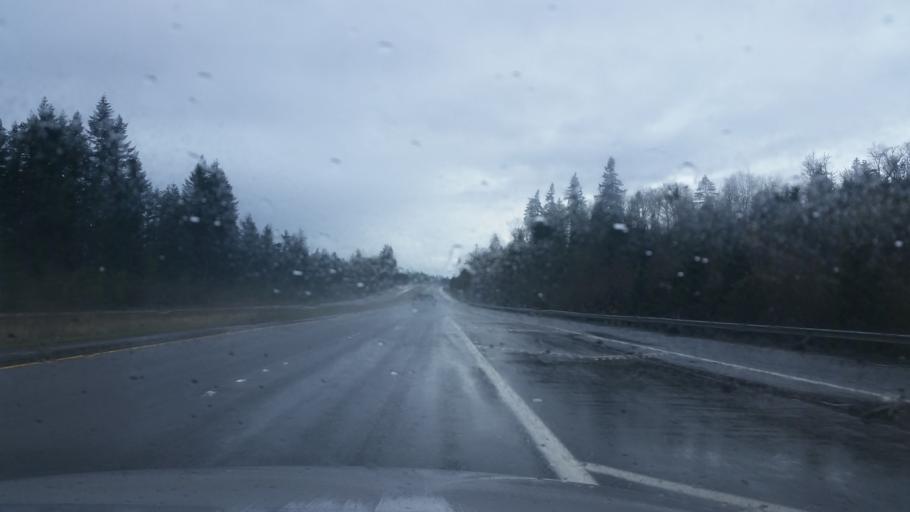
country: US
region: Washington
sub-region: King County
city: Maple Valley
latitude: 47.3924
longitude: -122.0509
